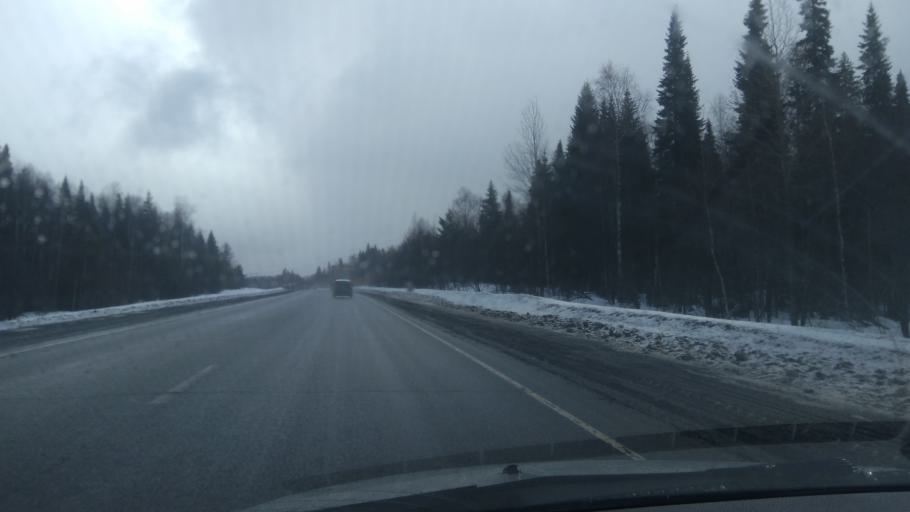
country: RU
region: Sverdlovsk
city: Arti
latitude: 56.7873
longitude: 58.5124
